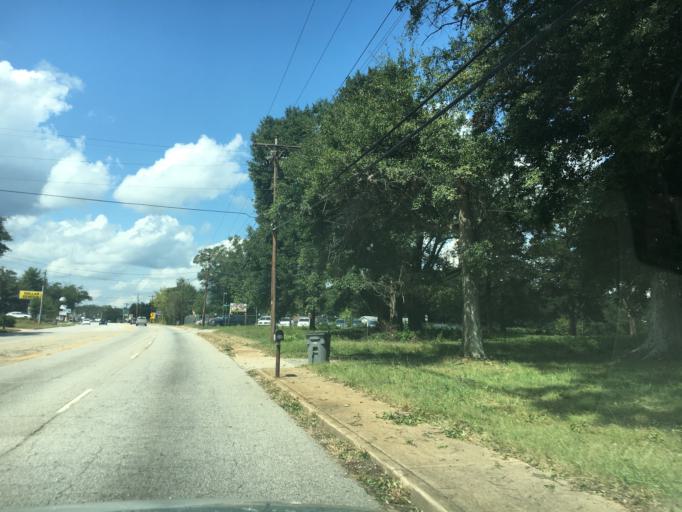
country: US
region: South Carolina
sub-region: Greenville County
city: Berea
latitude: 34.8815
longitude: -82.4502
